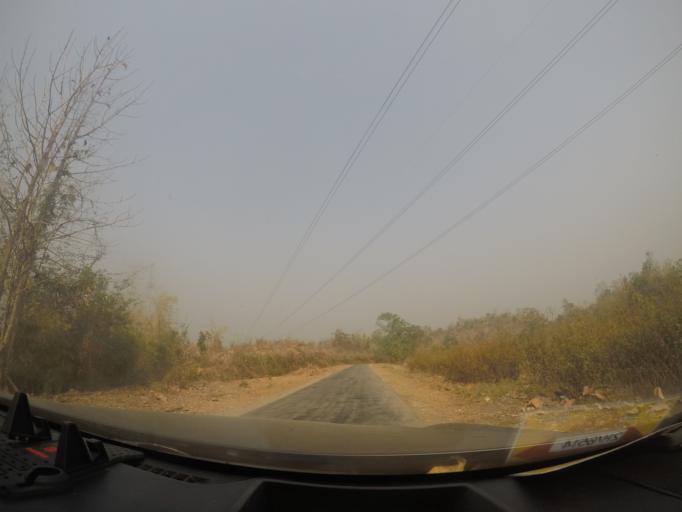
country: MM
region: Magway
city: Taungdwingyi
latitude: 19.9300
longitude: 95.8307
